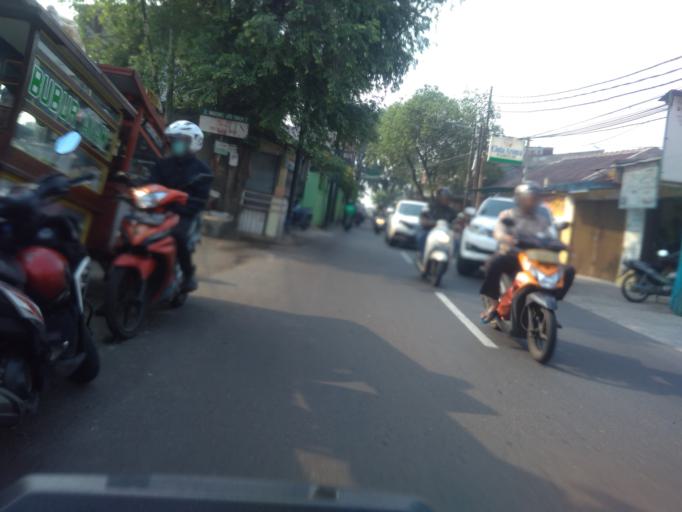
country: ID
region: Jakarta Raya
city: Jakarta
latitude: -6.2655
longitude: 106.8348
